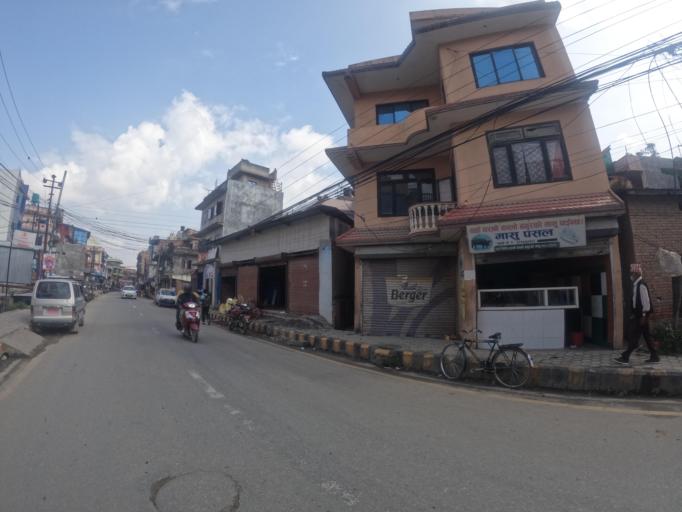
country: NP
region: Central Region
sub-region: Bagmati Zone
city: Patan
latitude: 27.6645
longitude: 85.3680
